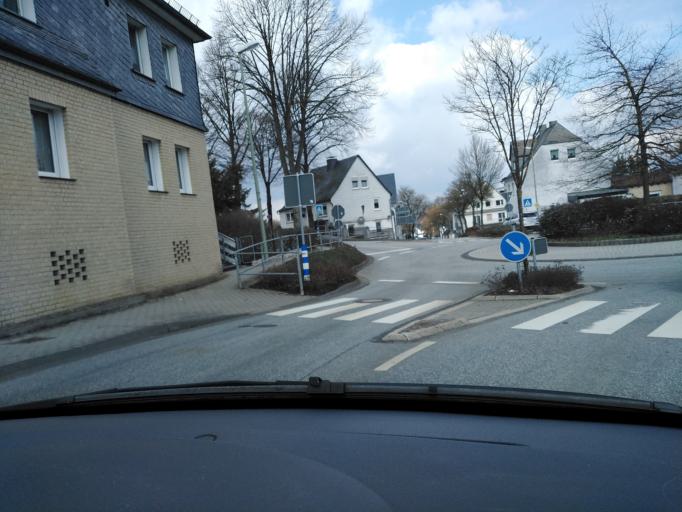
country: DE
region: North Rhine-Westphalia
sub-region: Regierungsbezirk Arnsberg
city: Brilon
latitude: 51.3909
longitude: 8.5720
